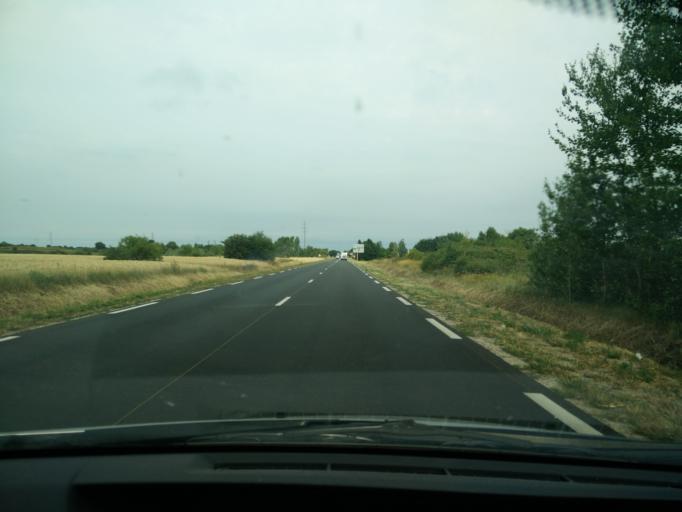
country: FR
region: Pays de la Loire
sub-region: Departement de Maine-et-Loire
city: Doue-la-Fontaine
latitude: 47.1800
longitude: -0.2413
